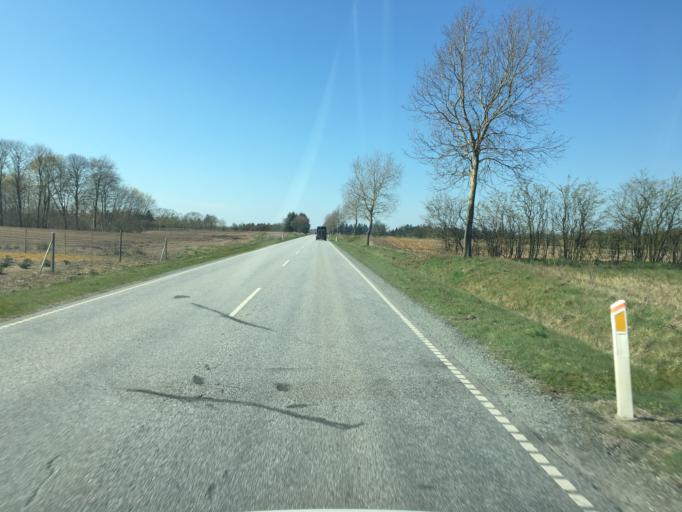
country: DK
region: South Denmark
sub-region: Aabenraa Kommune
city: Tinglev
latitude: 54.9447
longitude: 9.3556
